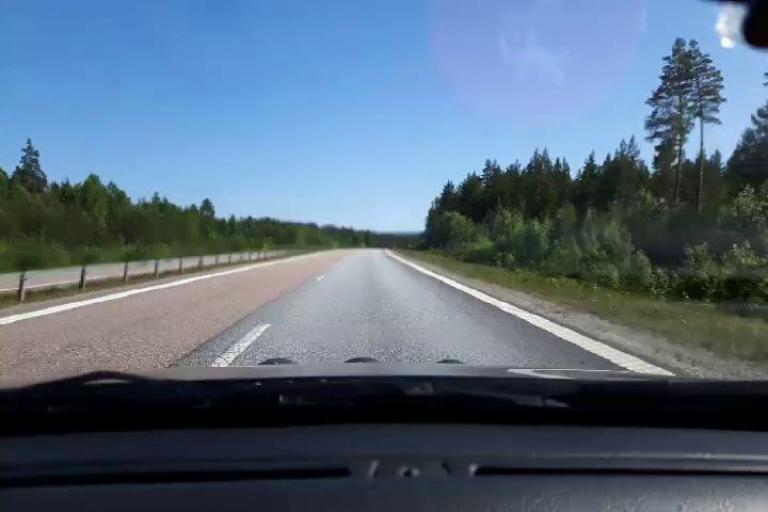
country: SE
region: Gaevleborg
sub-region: Soderhamns Kommun
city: Soderhamn
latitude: 61.3691
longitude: 17.0073
